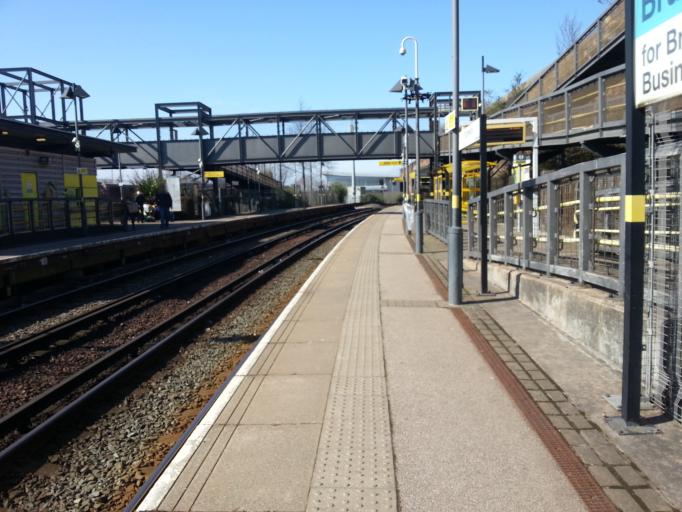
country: GB
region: England
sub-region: Liverpool
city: Liverpool
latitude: 53.3831
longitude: -2.9759
